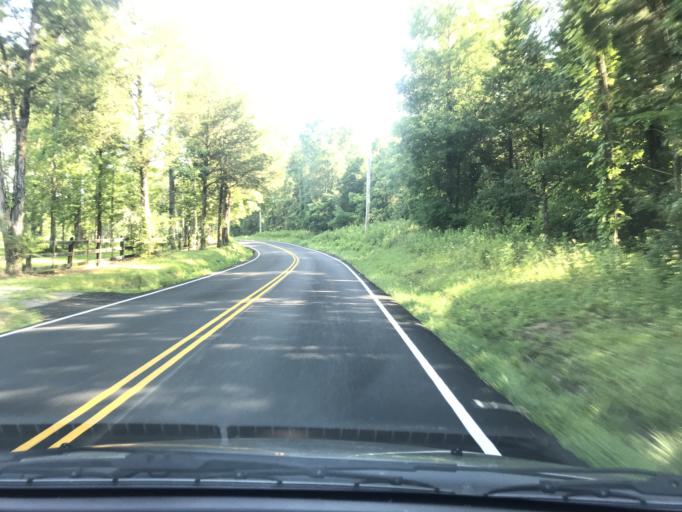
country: US
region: Tennessee
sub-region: Loudon County
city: Loudon
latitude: 35.7957
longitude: -84.3630
